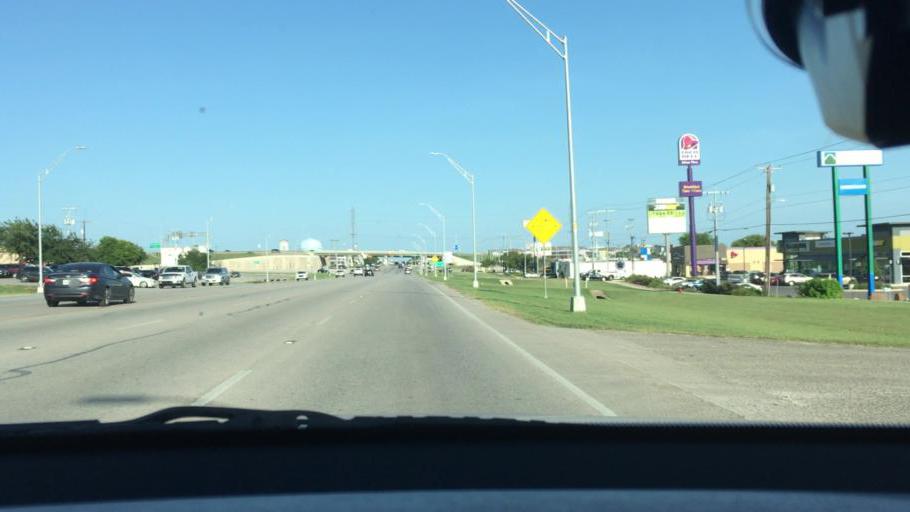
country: US
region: Texas
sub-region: Bexar County
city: Live Oak
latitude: 29.5625
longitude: -98.3320
